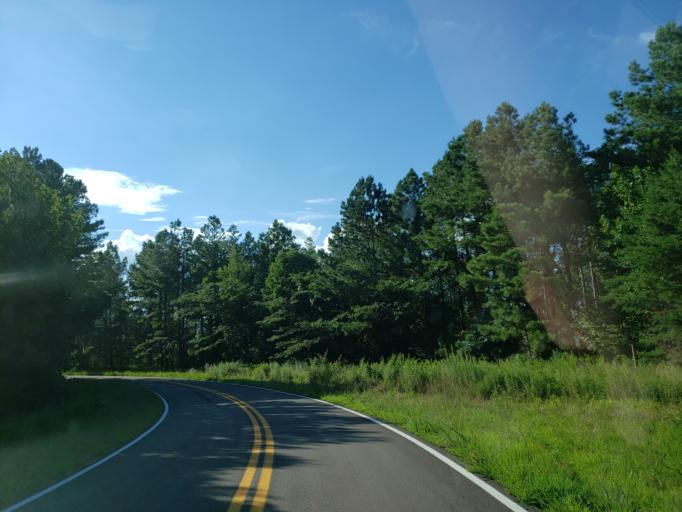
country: US
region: Georgia
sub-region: Bartow County
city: Rydal
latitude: 34.3749
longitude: -84.6293
